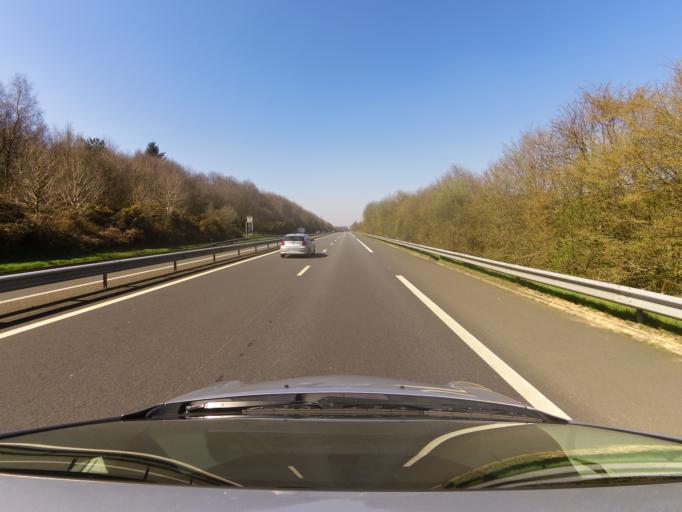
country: FR
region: Brittany
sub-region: Departement du Morbihan
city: Ploermel
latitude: 47.9185
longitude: -2.3754
